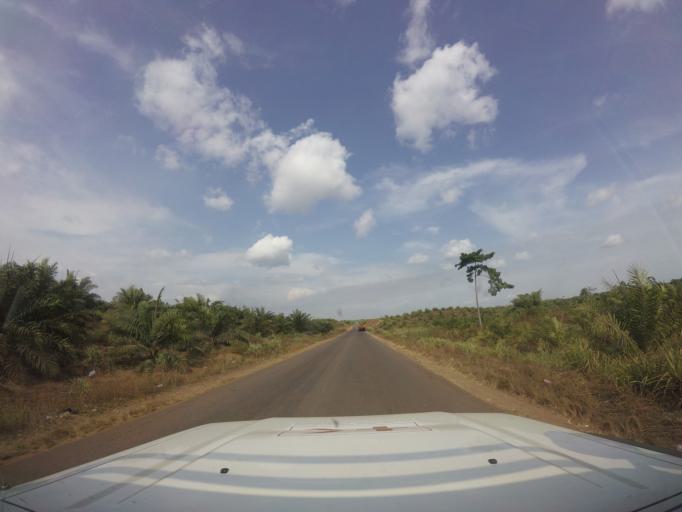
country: LR
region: Bomi
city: Tubmanburg
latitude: 6.7125
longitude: -10.9647
